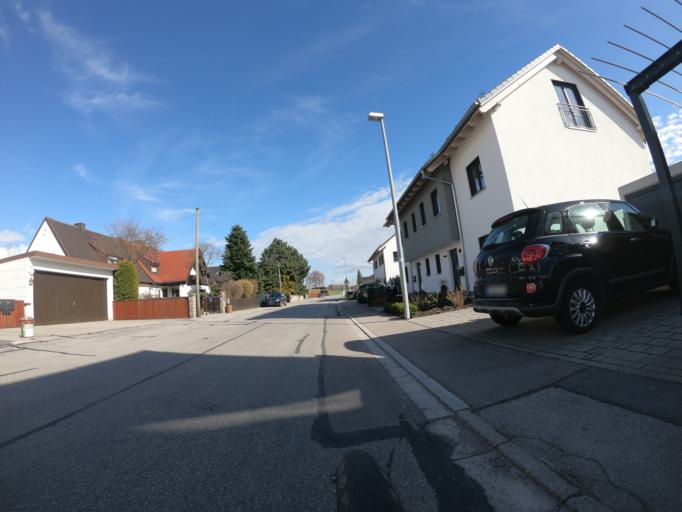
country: DE
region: Bavaria
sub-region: Upper Bavaria
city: Landsberied
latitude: 48.1792
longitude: 11.1916
